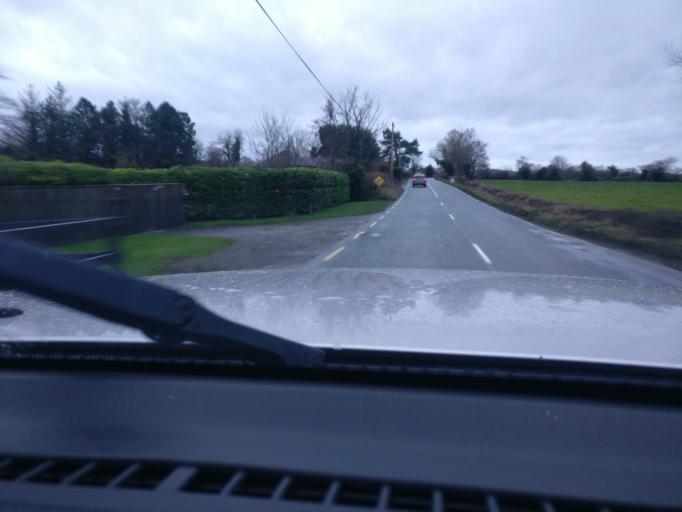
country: IE
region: Leinster
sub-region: An Mhi
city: Longwood
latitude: 53.4973
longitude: -6.8579
